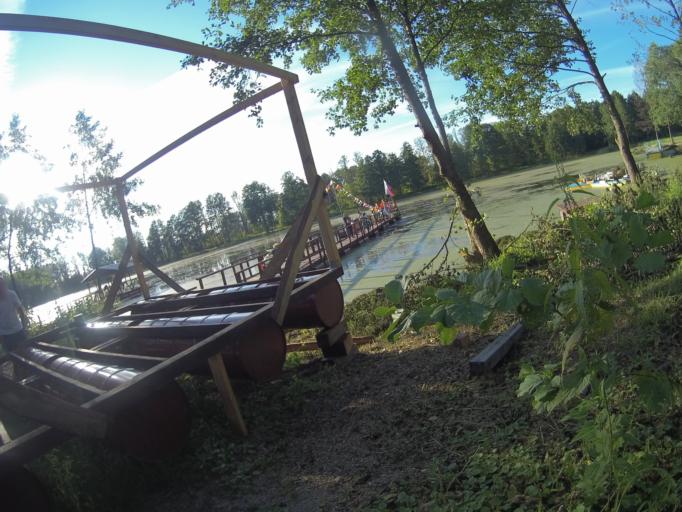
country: RU
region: Vladimir
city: Kommunar
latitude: 56.1008
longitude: 40.4346
